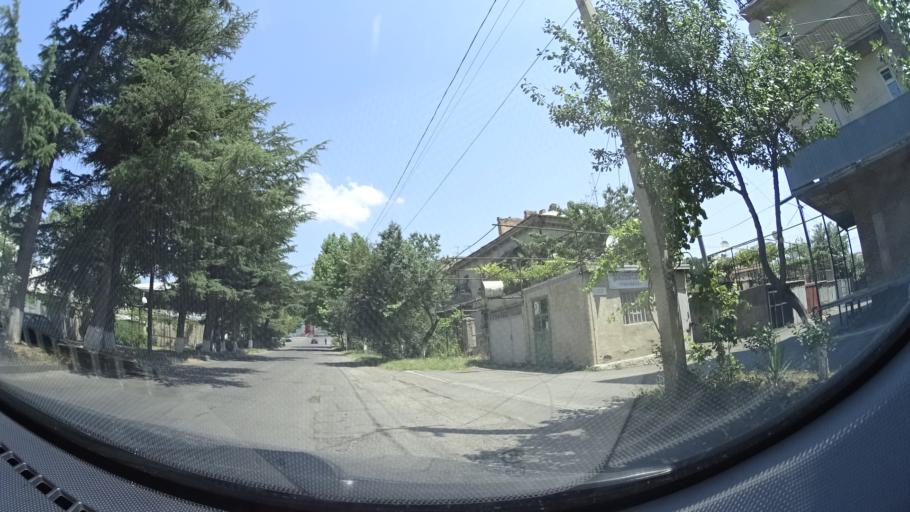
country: GE
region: Shida Kartli
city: Gori
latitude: 41.9897
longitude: 44.1191
